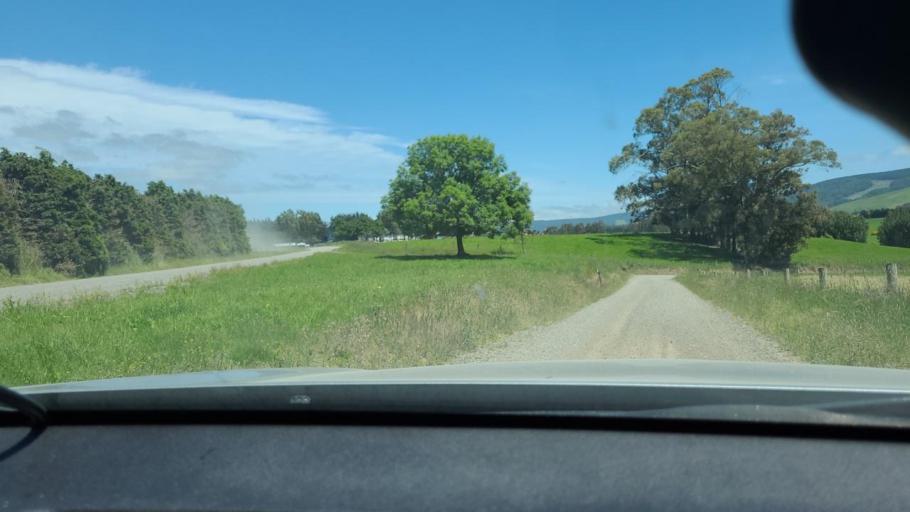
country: NZ
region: Southland
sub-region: Southland District
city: Riverton
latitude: -46.0267
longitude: 168.0118
